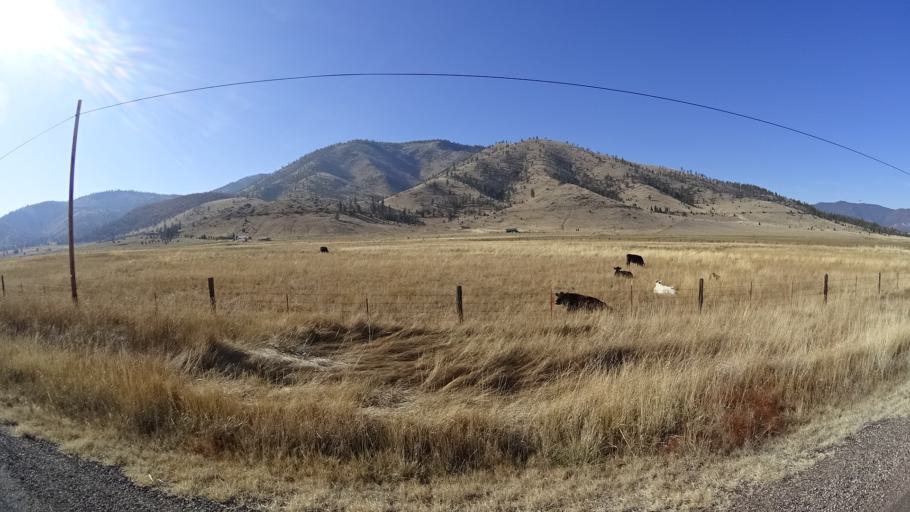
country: US
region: California
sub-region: Siskiyou County
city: Weed
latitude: 41.4846
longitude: -122.4973
